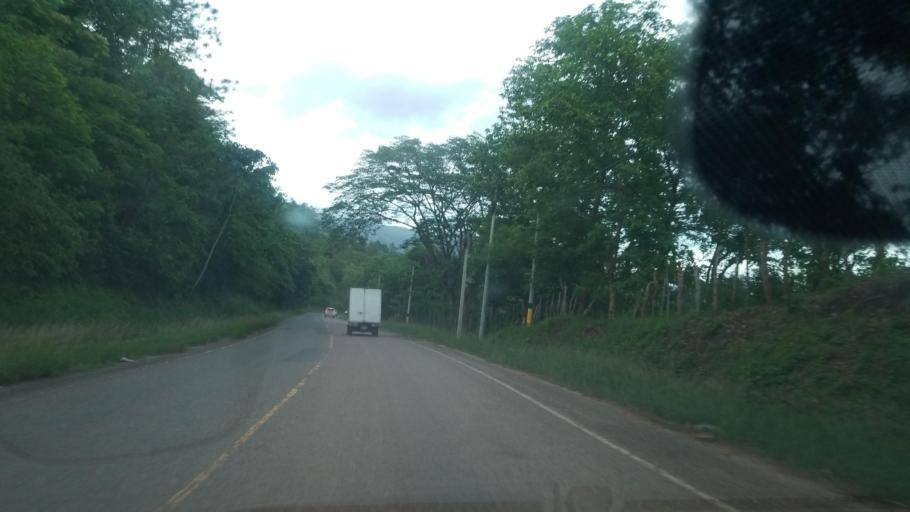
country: HN
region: Santa Barbara
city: Concepcion del Sur
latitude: 14.7990
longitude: -88.1481
